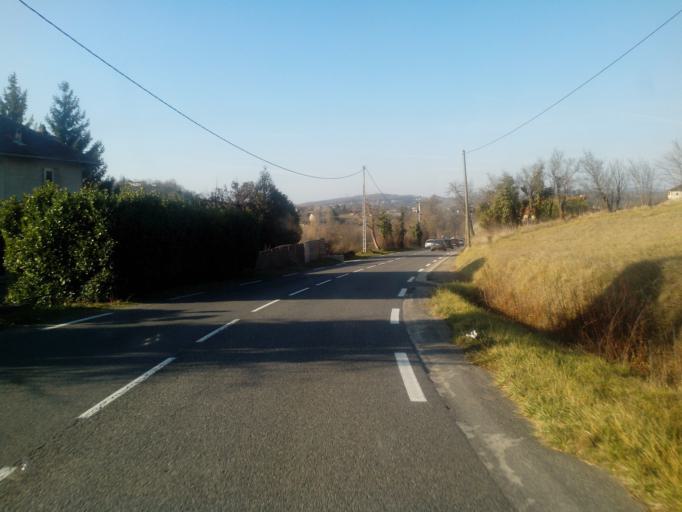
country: FR
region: Midi-Pyrenees
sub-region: Departement du Lot
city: Figeac
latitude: 44.6021
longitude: 2.0583
